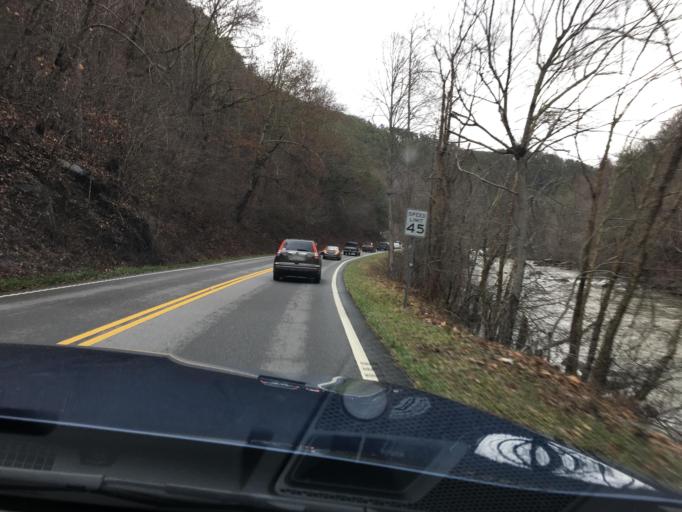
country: US
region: Georgia
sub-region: Fannin County
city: McCaysville
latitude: 35.0805
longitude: -84.4951
